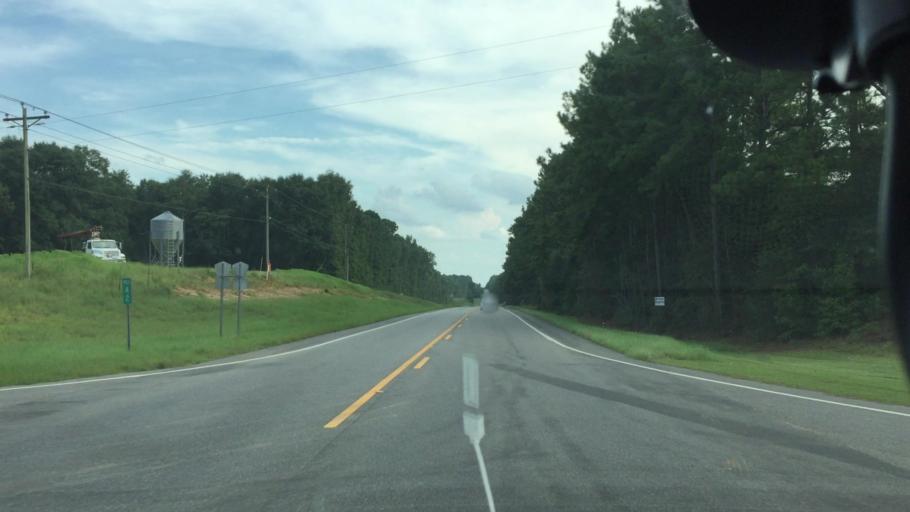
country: US
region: Alabama
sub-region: Coffee County
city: New Brockton
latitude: 31.5331
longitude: -85.9181
